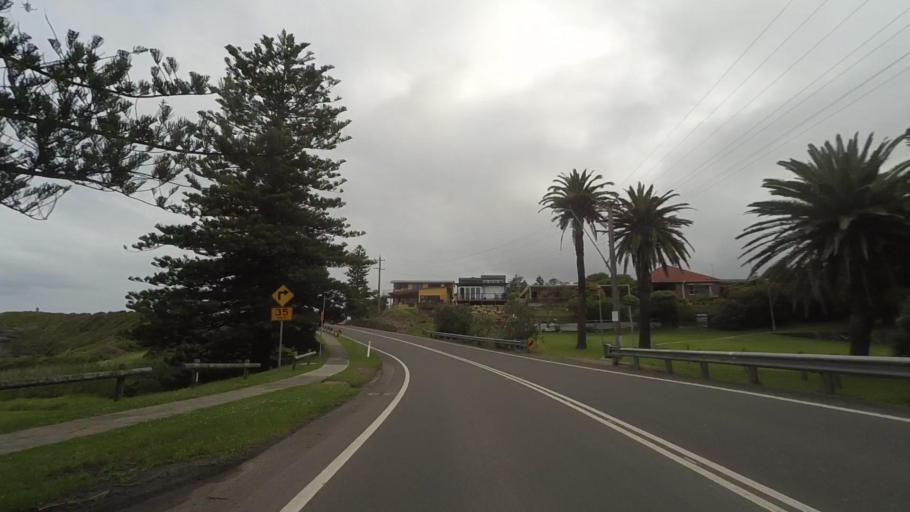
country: AU
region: New South Wales
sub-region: Wollongong
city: Bulli
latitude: -34.3040
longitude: 150.9371
